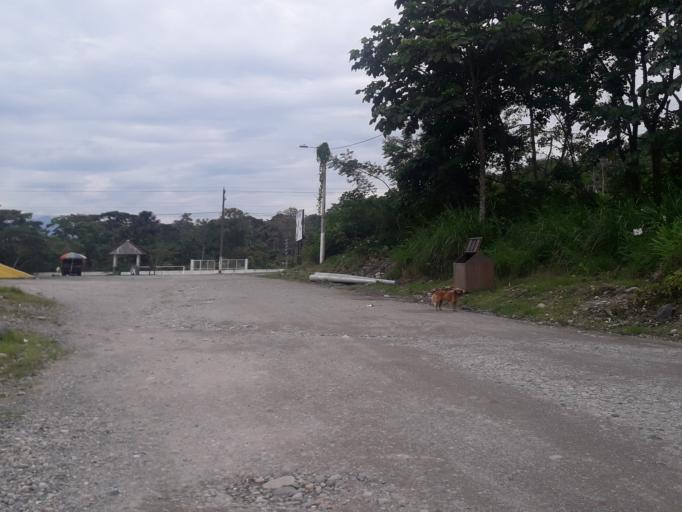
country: EC
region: Napo
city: Tena
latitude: -1.0431
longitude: -77.7962
